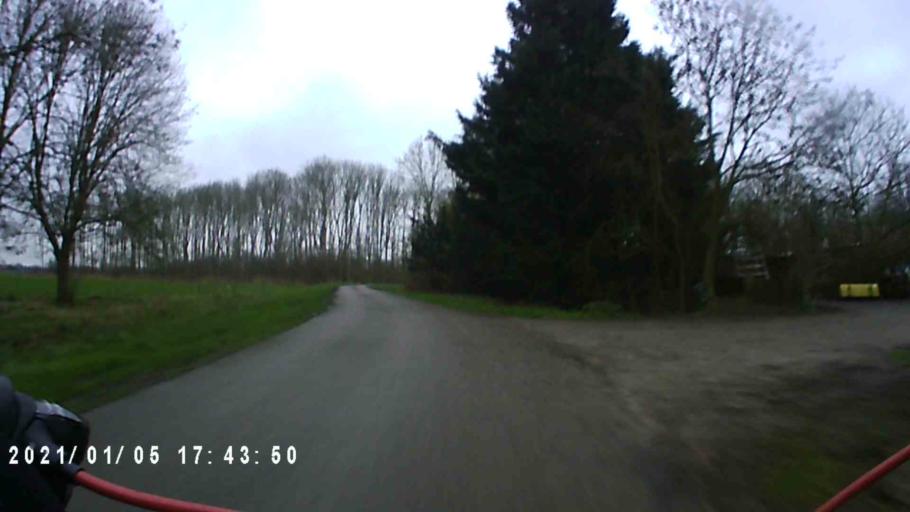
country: NL
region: Groningen
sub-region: Gemeente Slochteren
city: Slochteren
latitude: 53.2129
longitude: 6.9085
